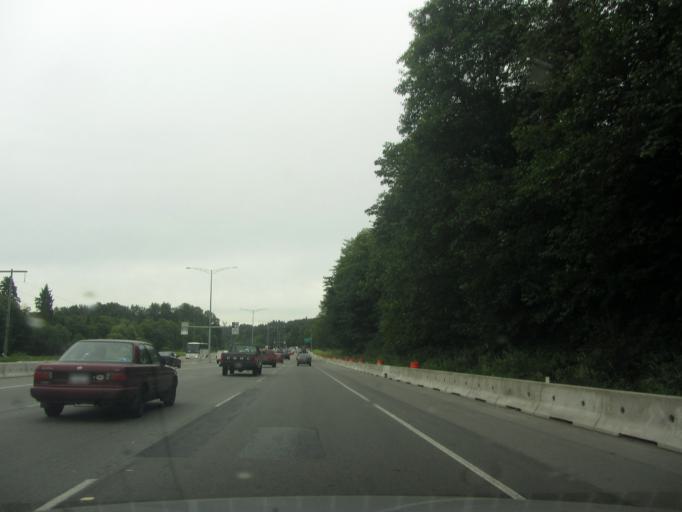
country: CA
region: British Columbia
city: Burnaby
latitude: 49.2551
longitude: -122.9782
